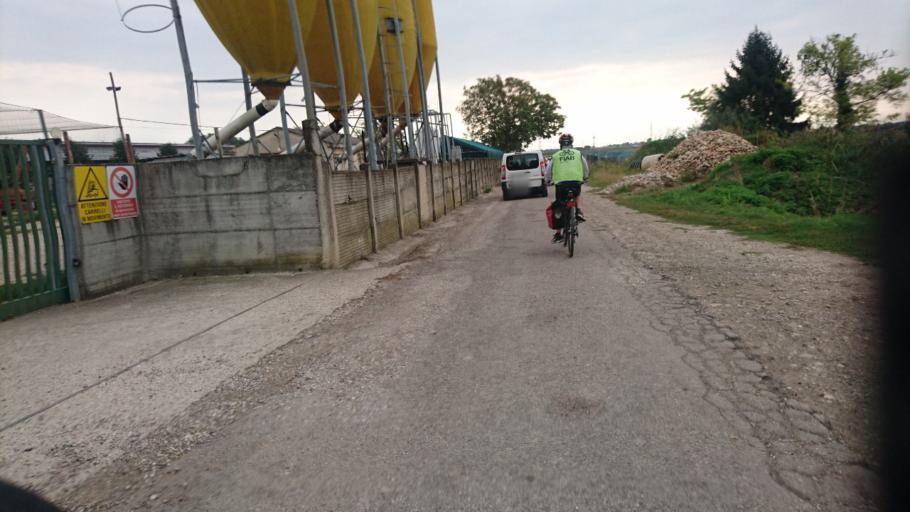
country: IT
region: Veneto
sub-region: Provincia di Verona
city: San Martino Buon Albergo
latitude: 45.4056
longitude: 11.1079
